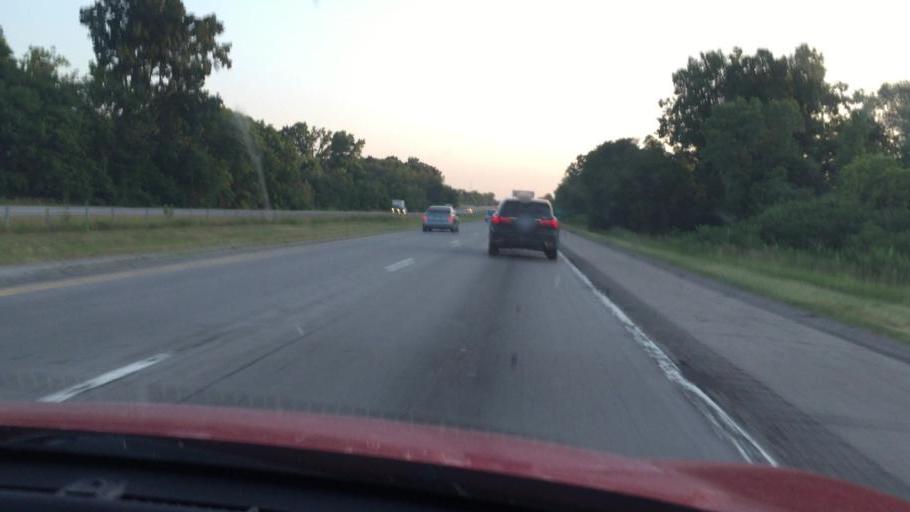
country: US
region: Michigan
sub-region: Washtenaw County
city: Milan
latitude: 42.1470
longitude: -83.6835
